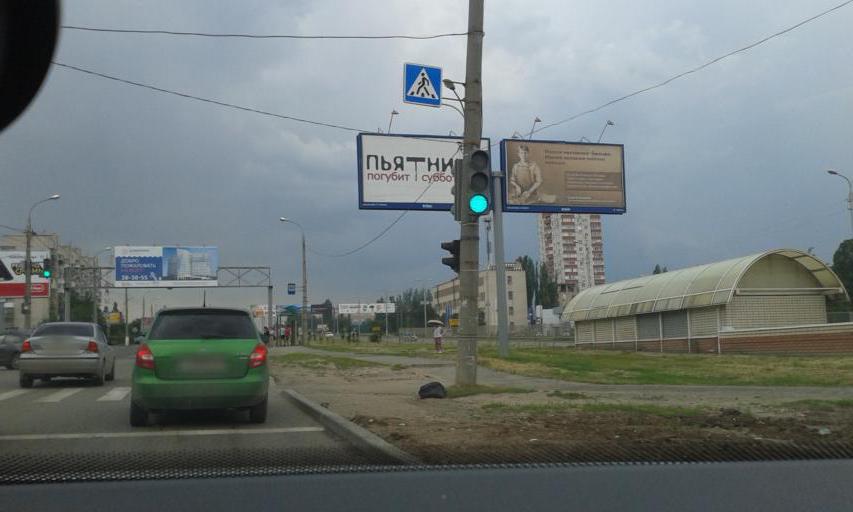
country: RU
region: Volgograd
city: Volgograd
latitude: 48.7569
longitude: 44.4931
